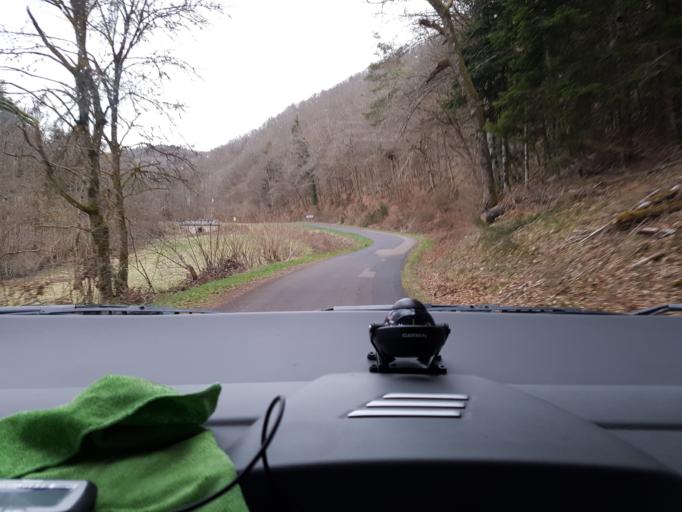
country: FR
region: Auvergne
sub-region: Departement du Puy-de-Dome
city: Chapdes-Beaufort
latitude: 45.8674
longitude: 2.8184
